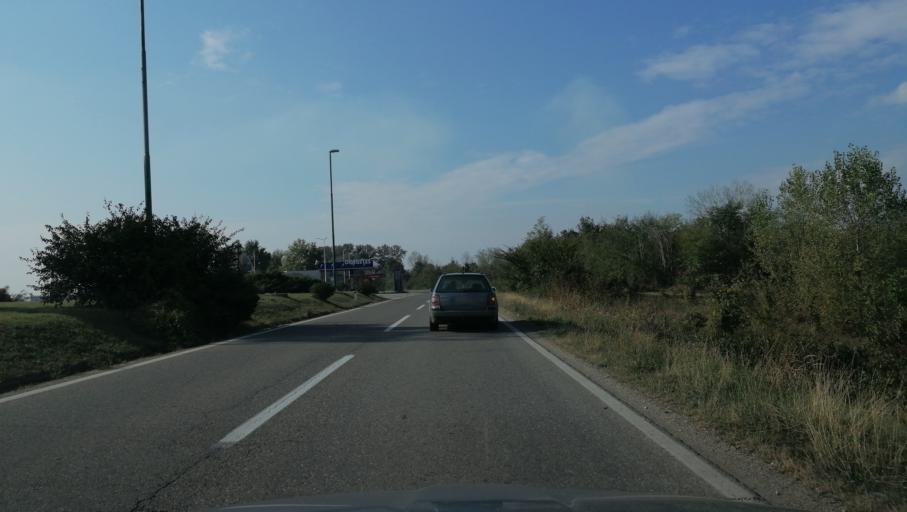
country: BA
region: Republika Srpska
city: Popovi
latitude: 44.7792
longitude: 19.3186
